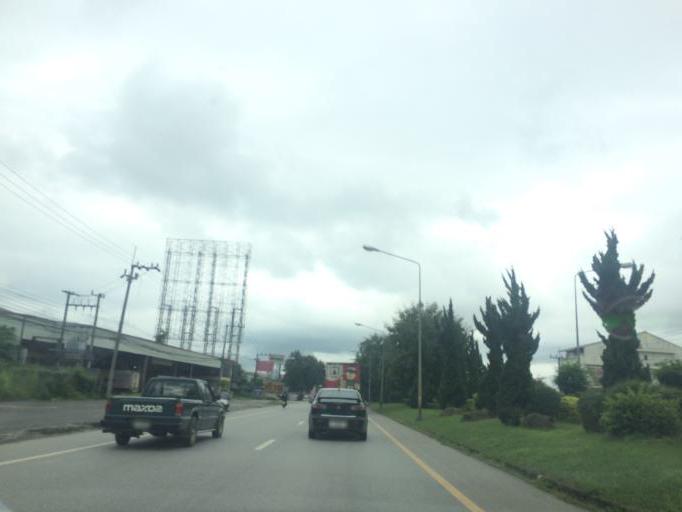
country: TH
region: Chiang Rai
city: Chiang Rai
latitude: 19.8659
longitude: 99.8232
